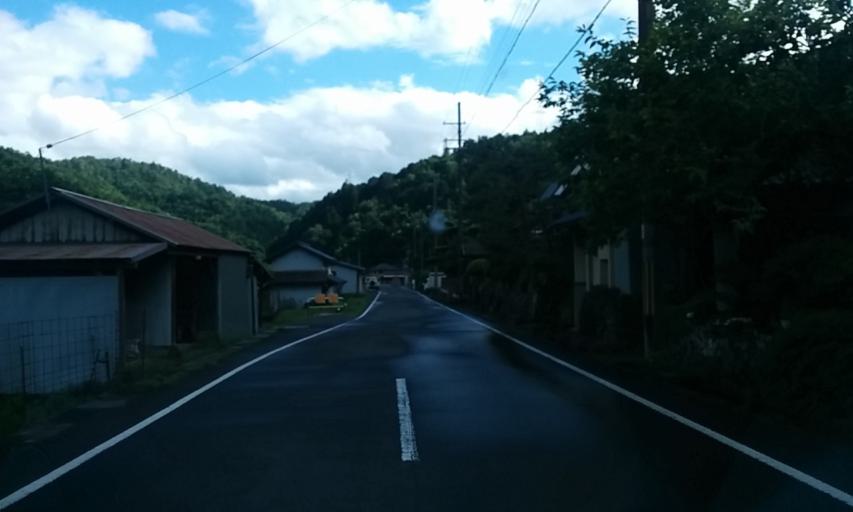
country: JP
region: Kyoto
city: Ayabe
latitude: 35.3878
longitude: 135.2577
